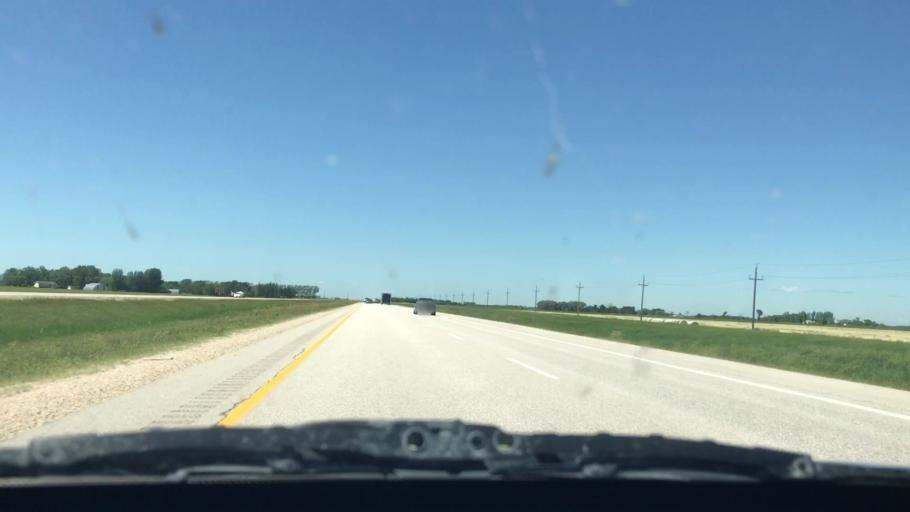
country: CA
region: Manitoba
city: Steinbach
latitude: 49.7285
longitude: -96.7143
